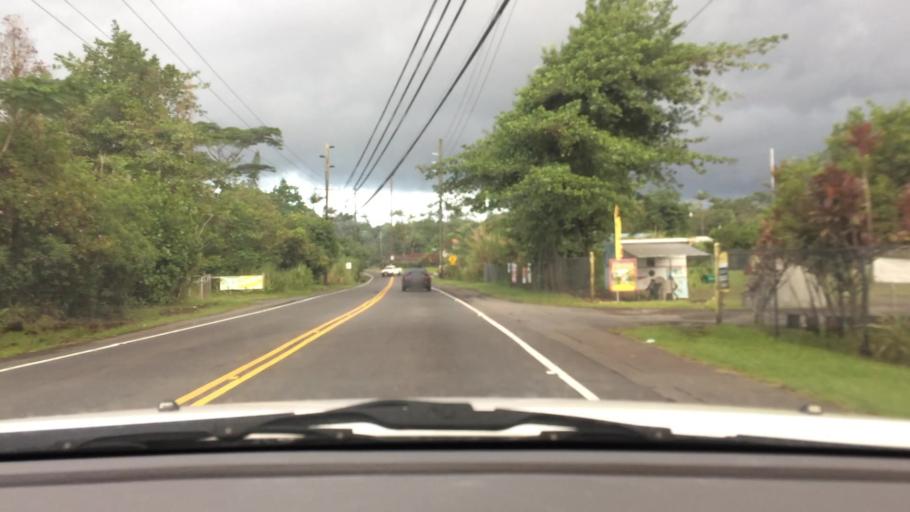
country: US
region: Hawaii
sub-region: Hawaii County
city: Hawaiian Paradise Park
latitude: 19.5005
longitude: -154.9544
